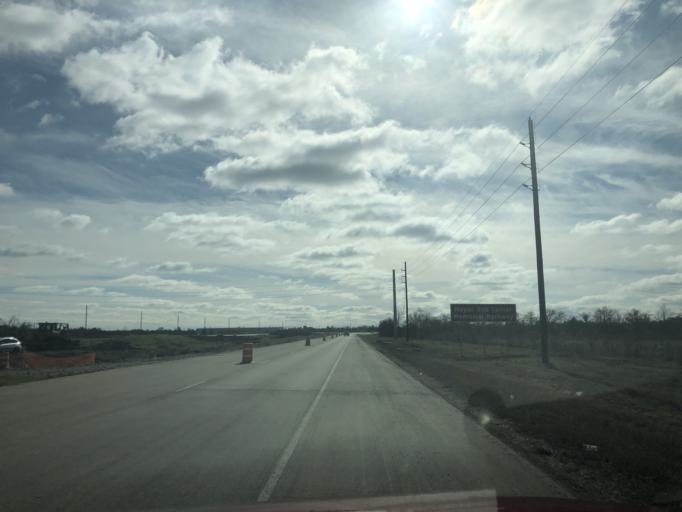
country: US
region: Texas
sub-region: Chambers County
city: Mont Belvieu
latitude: 29.8210
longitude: -94.8648
